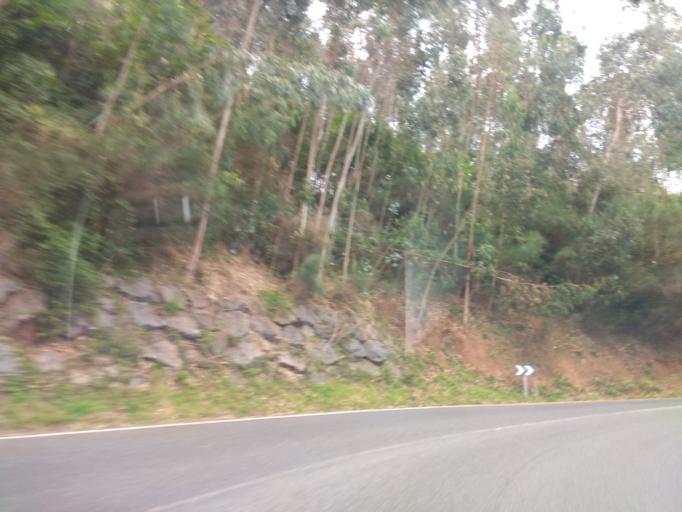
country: ES
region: Cantabria
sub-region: Provincia de Cantabria
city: Hazas de Cesto
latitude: 43.4039
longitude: -3.6004
